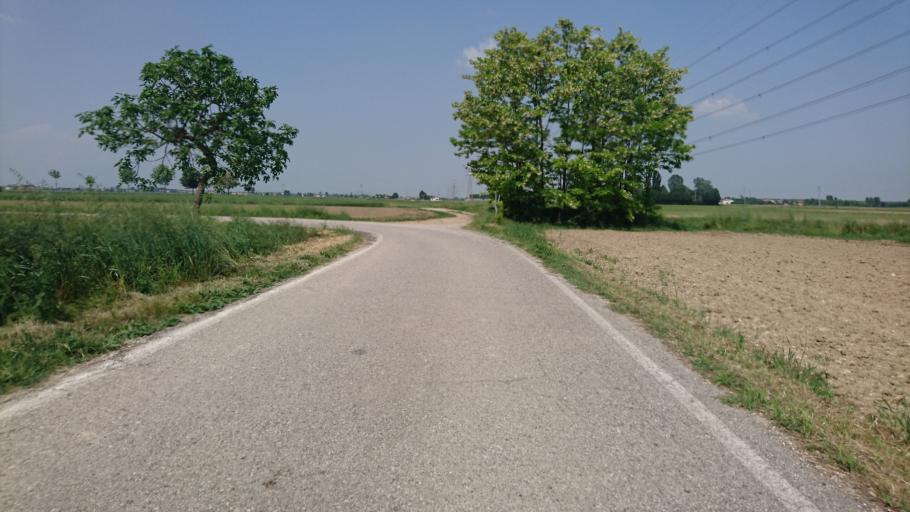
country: IT
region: Veneto
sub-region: Provincia di Venezia
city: Campagna Lupia
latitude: 45.3698
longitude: 12.1238
